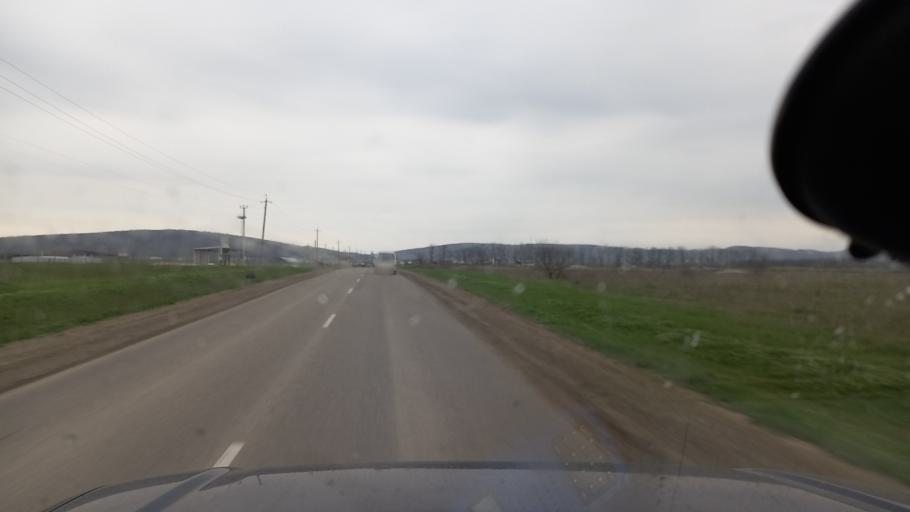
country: RU
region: Krasnodarskiy
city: Anapskaya
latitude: 44.8822
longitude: 37.4513
